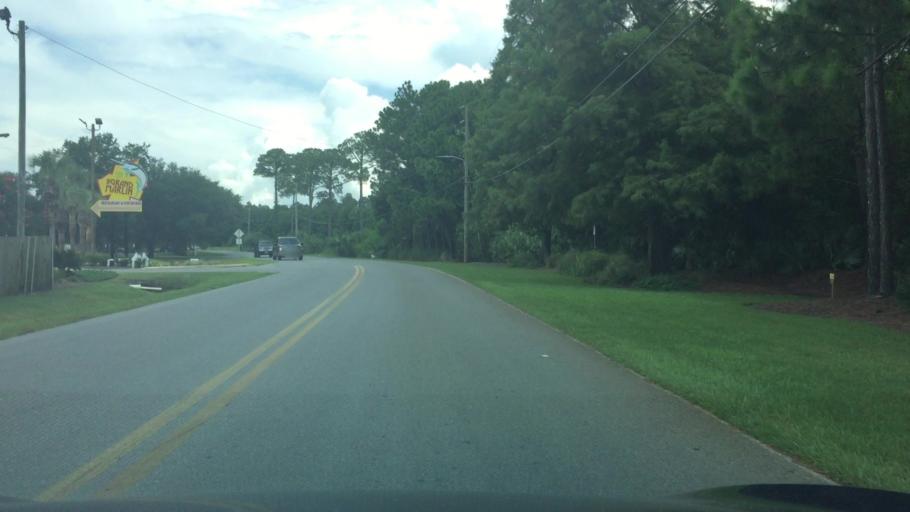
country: US
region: Florida
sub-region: Bay County
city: Lower Grand Lagoon
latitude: 30.1493
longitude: -85.7441
